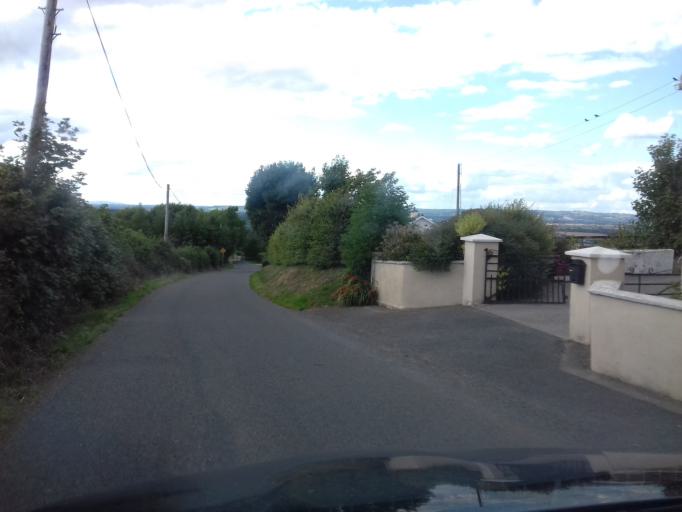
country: IE
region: Leinster
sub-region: Kilkenny
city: Graiguenamanagh
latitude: 52.5788
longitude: -7.0118
